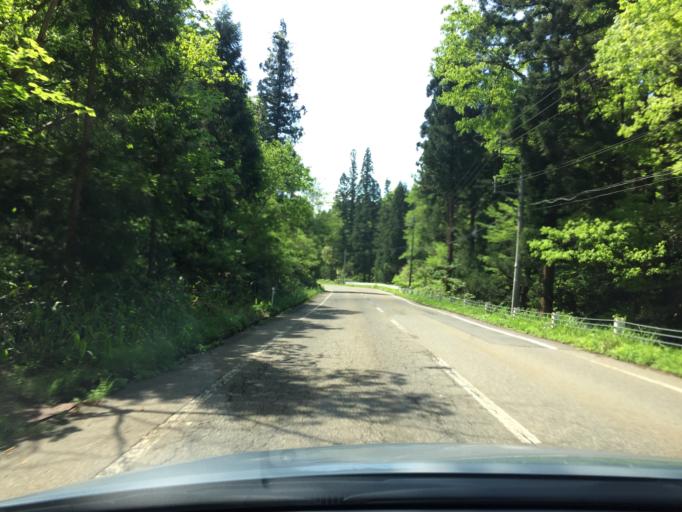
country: JP
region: Niigata
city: Tochio-honcho
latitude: 37.5331
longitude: 139.0924
